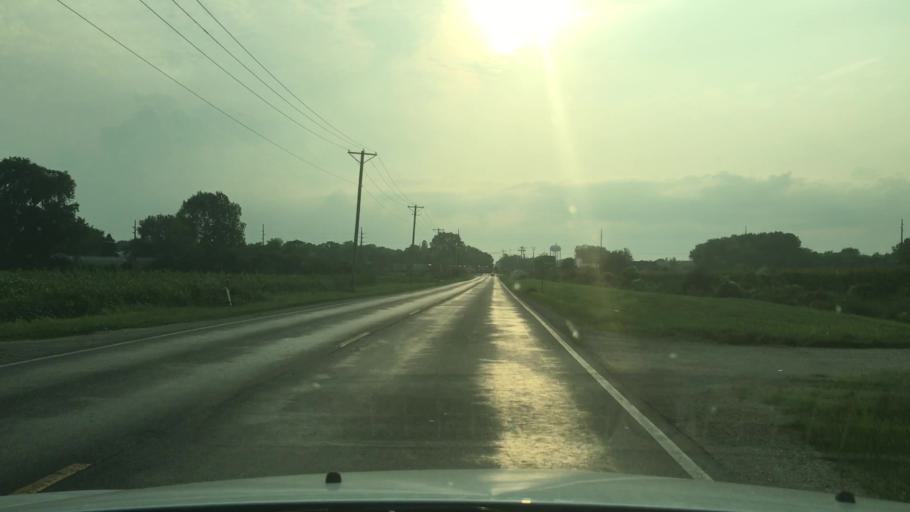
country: US
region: Illinois
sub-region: Ogle County
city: Rochelle
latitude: 41.9198
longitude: -89.0501
